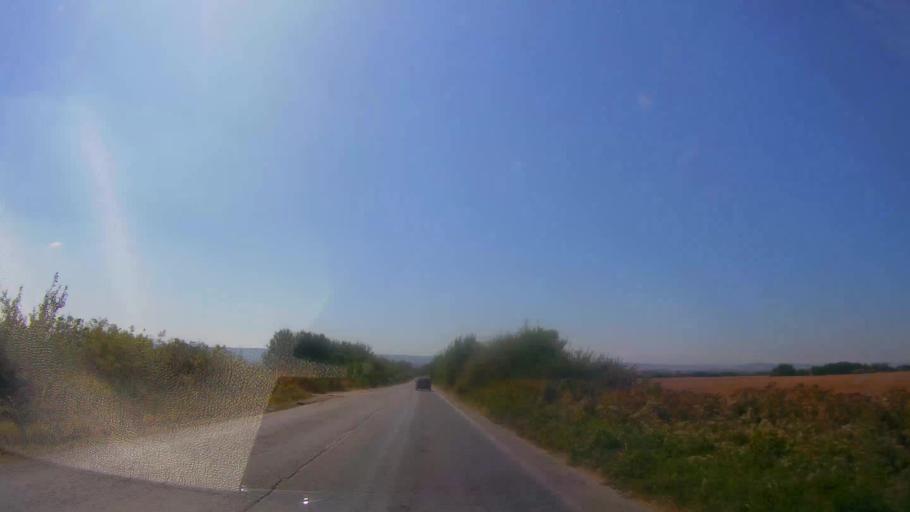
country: BG
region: Veliko Turnovo
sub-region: Obshtina Gorna Oryakhovitsa
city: Purvomaytsi
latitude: 43.2251
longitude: 25.6379
